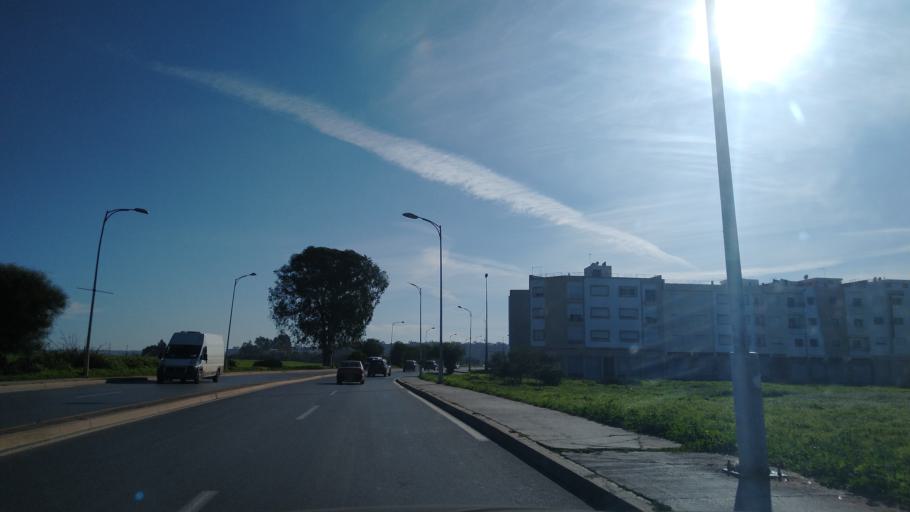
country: MA
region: Rabat-Sale-Zemmour-Zaer
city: Sale
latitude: 34.0175
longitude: -6.7348
